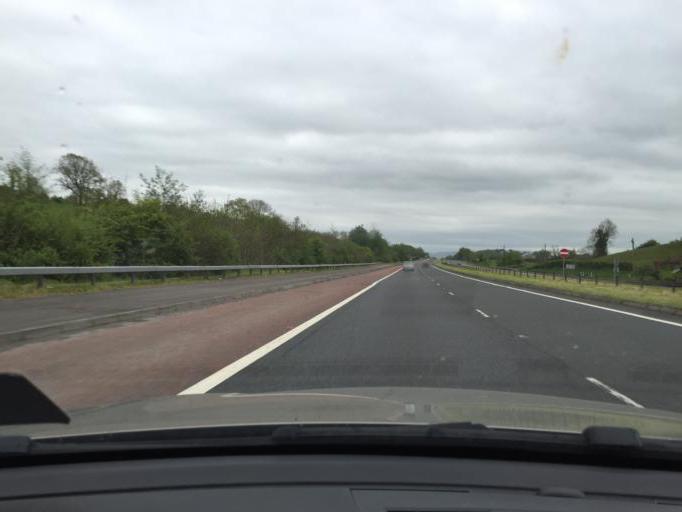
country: GB
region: Northern Ireland
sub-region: Banbridge District
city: Banbridge
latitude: 54.2757
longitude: -6.3073
